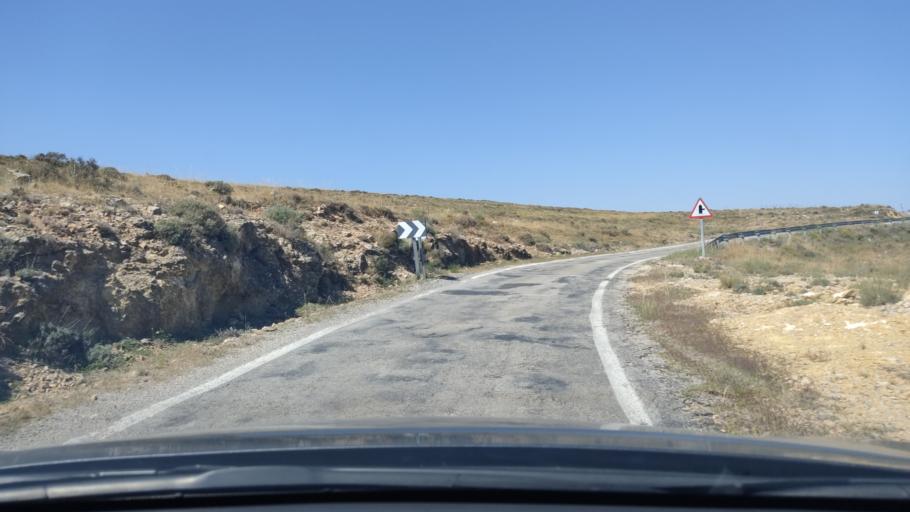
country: ES
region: Aragon
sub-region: Provincia de Teruel
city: Huesa del Comun
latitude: 41.0192
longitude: -0.9580
